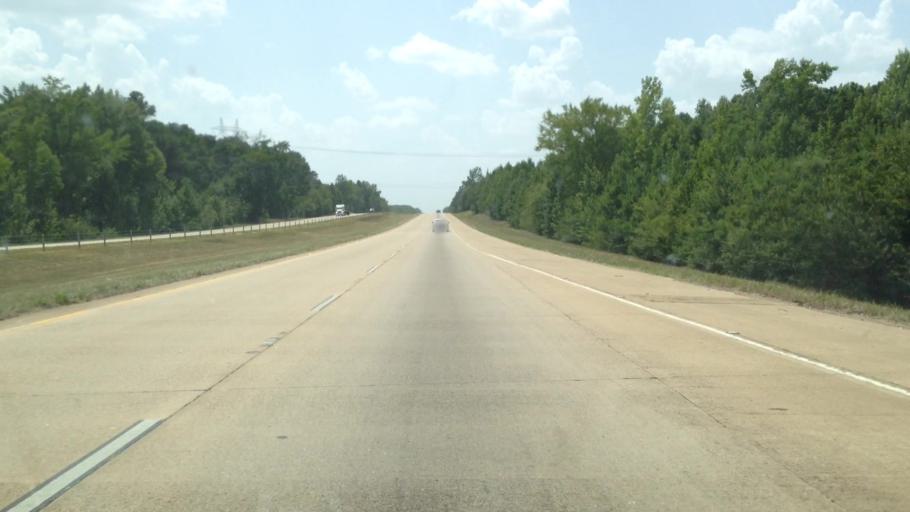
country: US
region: Louisiana
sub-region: Lincoln Parish
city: Grambling
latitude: 32.5423
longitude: -92.7194
